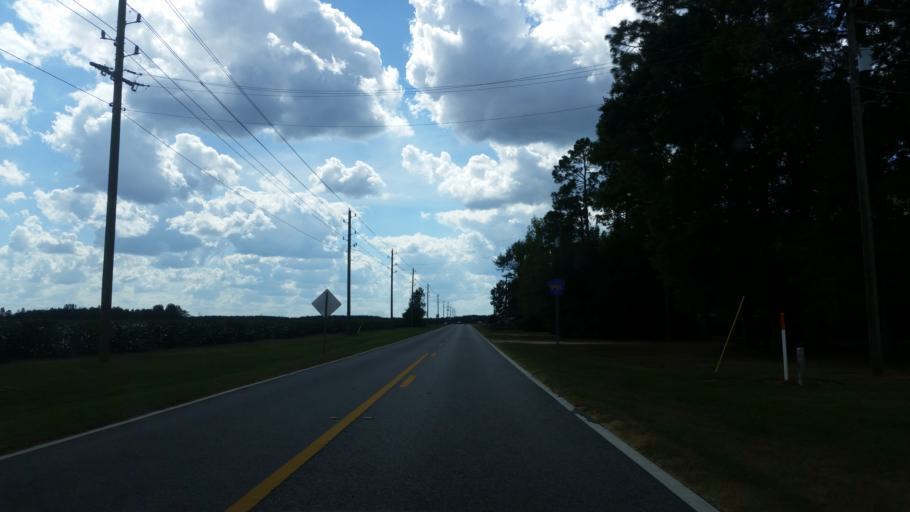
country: US
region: Alabama
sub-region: Escambia County
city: Atmore
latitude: 30.8950
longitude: -87.4764
